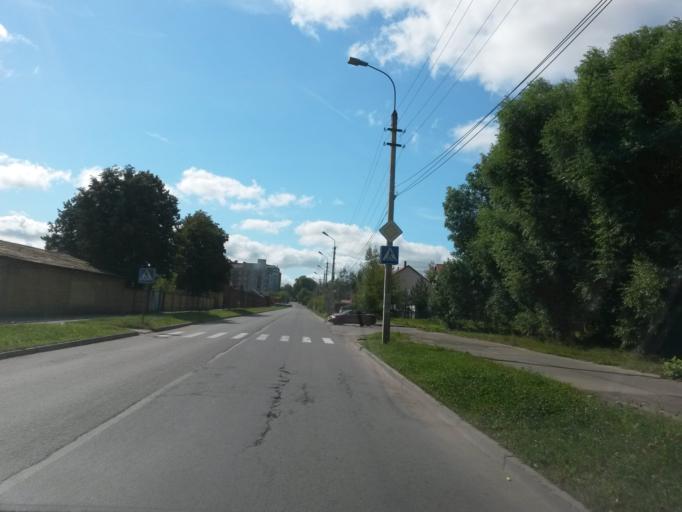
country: RU
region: Jaroslavl
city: Yaroslavl
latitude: 57.6086
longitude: 39.8734
